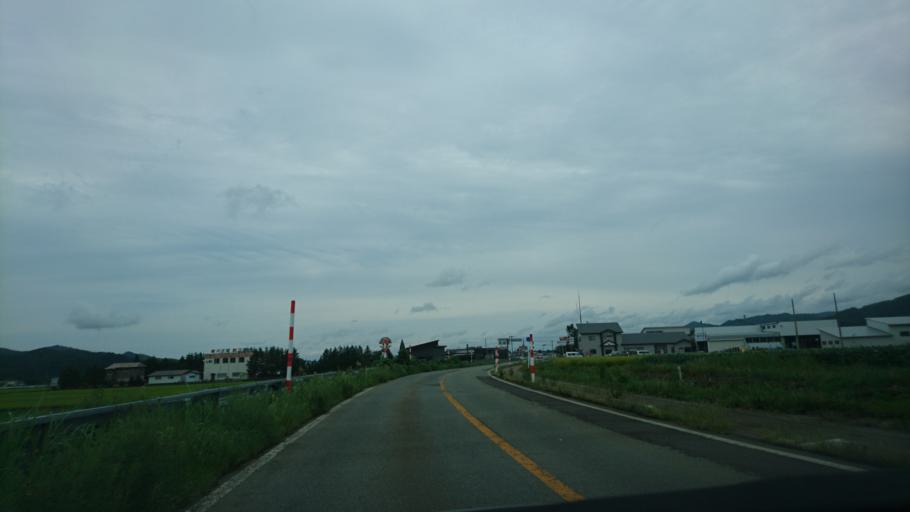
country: JP
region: Akita
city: Yuzawa
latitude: 39.1585
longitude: 140.5641
